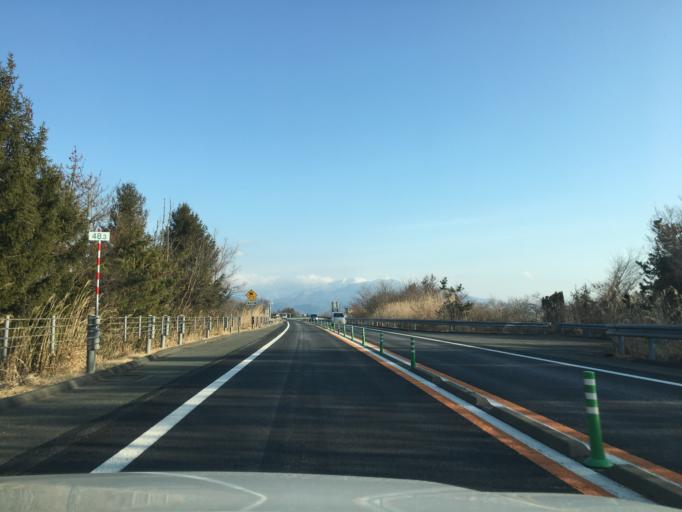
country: JP
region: Yamagata
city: Sagae
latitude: 38.3209
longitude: 140.3013
